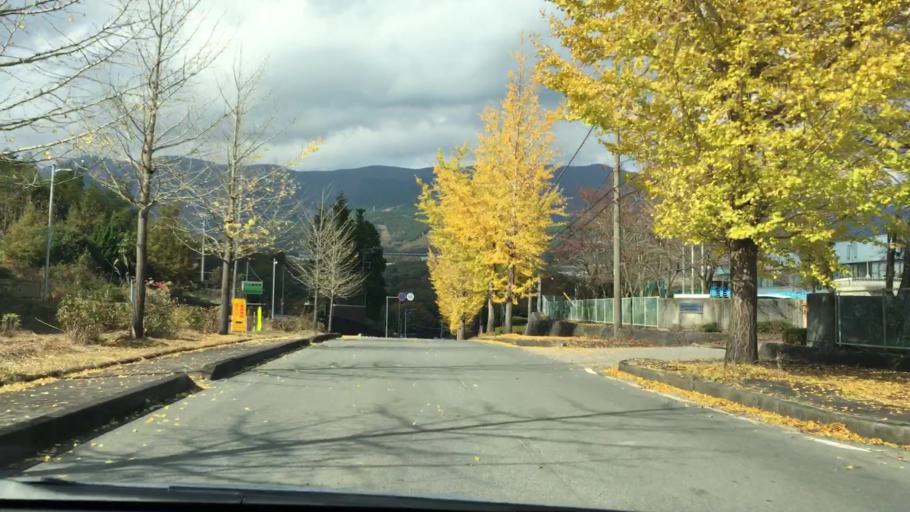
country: JP
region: Shizuoka
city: Gotemba
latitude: 35.3570
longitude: 138.9439
